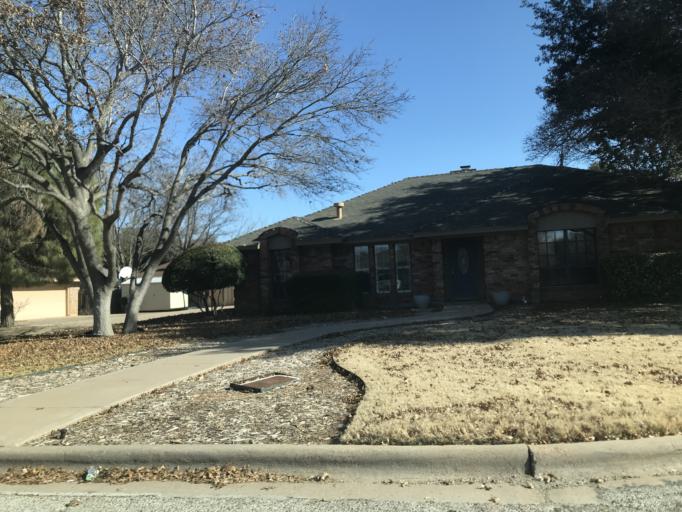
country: US
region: Texas
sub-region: Taylor County
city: Abilene
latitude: 32.3812
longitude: -99.7575
